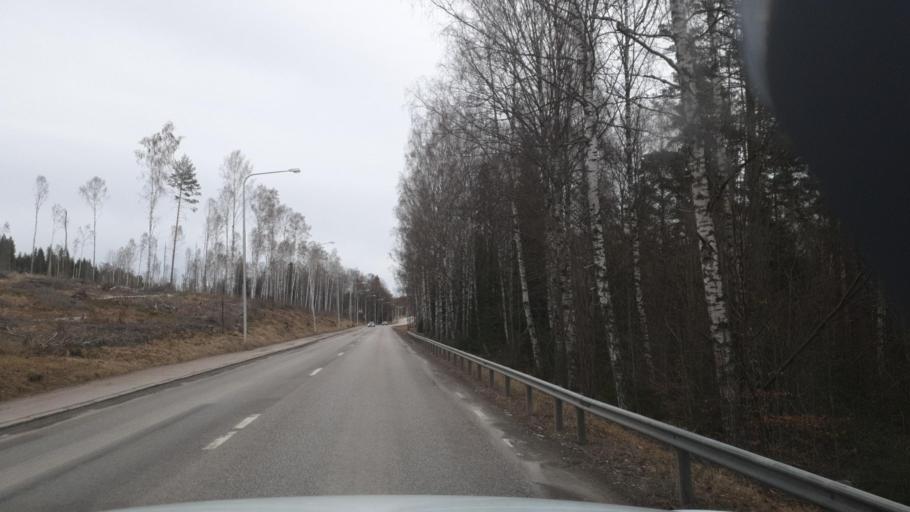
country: SE
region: Vaermland
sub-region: Arvika Kommun
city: Arvika
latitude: 59.6700
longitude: 12.4813
